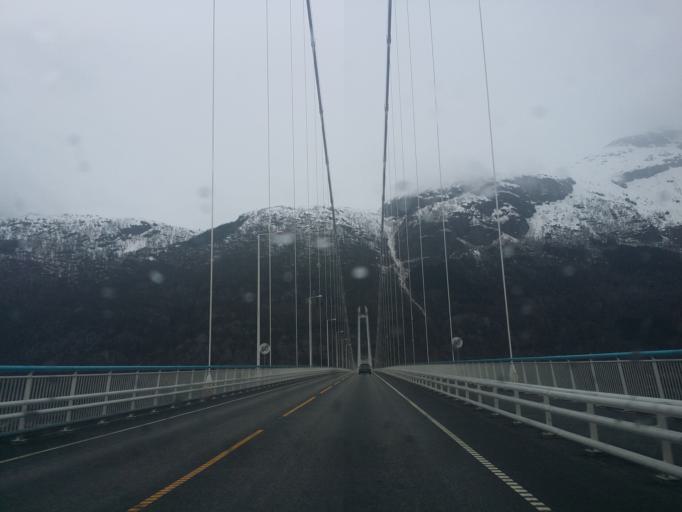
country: NO
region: Hordaland
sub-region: Ulvik
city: Ulvik
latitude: 60.4743
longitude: 6.8352
